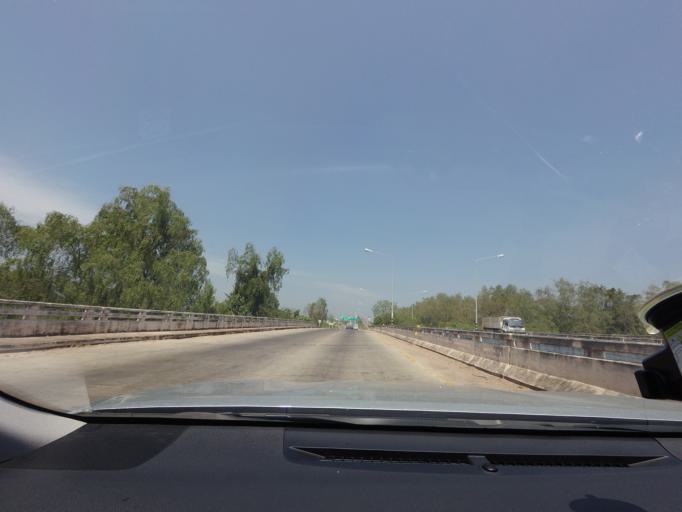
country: TH
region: Surat Thani
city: Surat Thani
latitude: 9.1685
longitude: 99.3657
